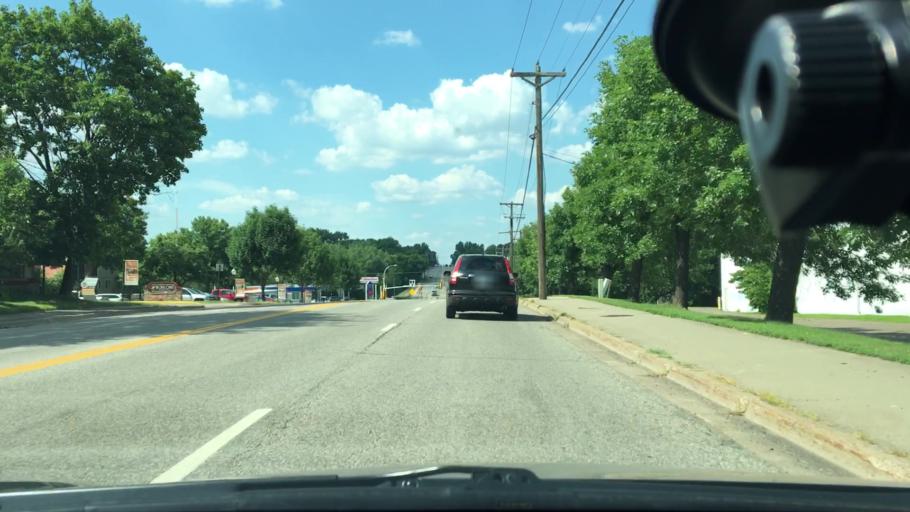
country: US
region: Minnesota
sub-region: Hennepin County
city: New Hope
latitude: 45.0199
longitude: -93.3802
